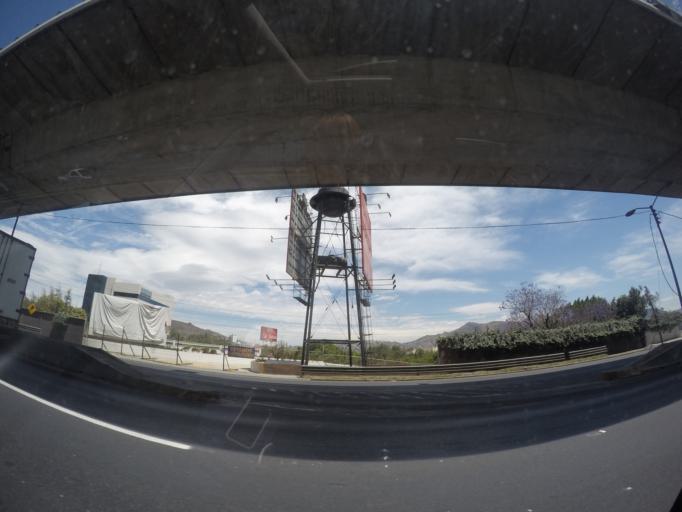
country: MX
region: Mexico
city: Tlalnepantla
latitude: 19.5787
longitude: -99.2068
